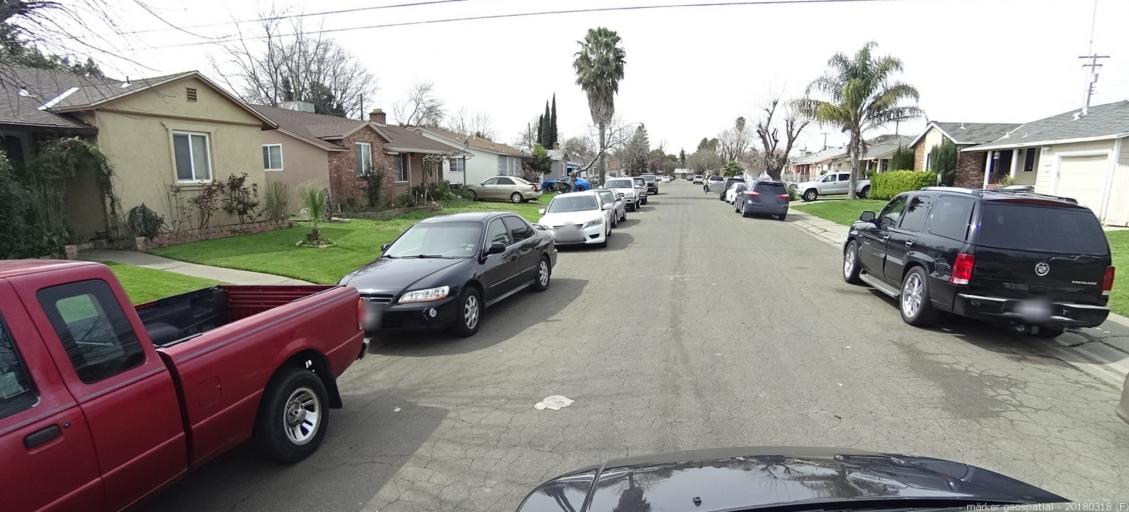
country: US
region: California
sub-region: Sacramento County
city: Parkway
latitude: 38.5192
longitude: -121.4513
